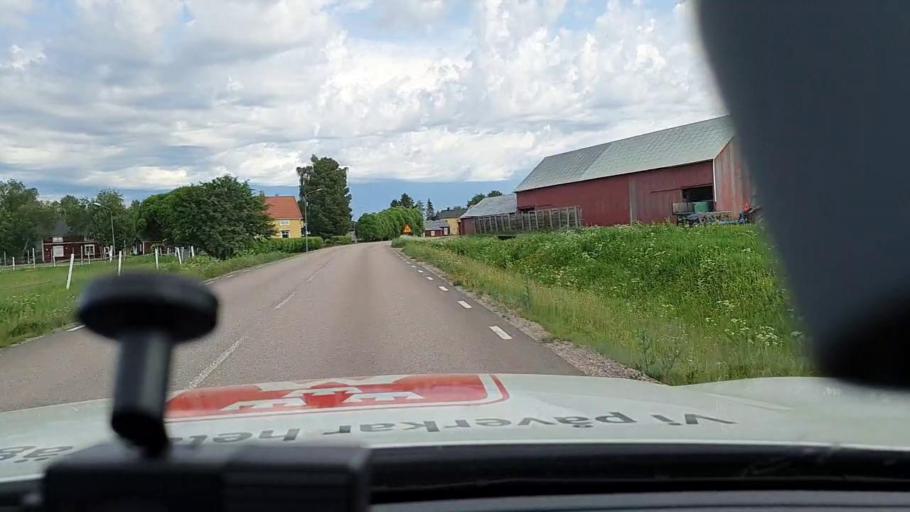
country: SE
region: Norrbotten
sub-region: Bodens Kommun
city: Saevast
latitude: 65.7081
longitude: 21.7612
